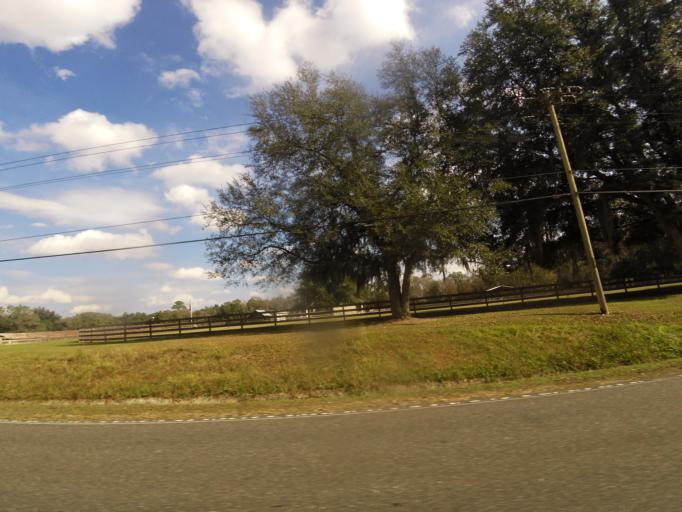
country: US
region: Florida
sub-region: Duval County
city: Baldwin
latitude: 30.1829
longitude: -81.9916
